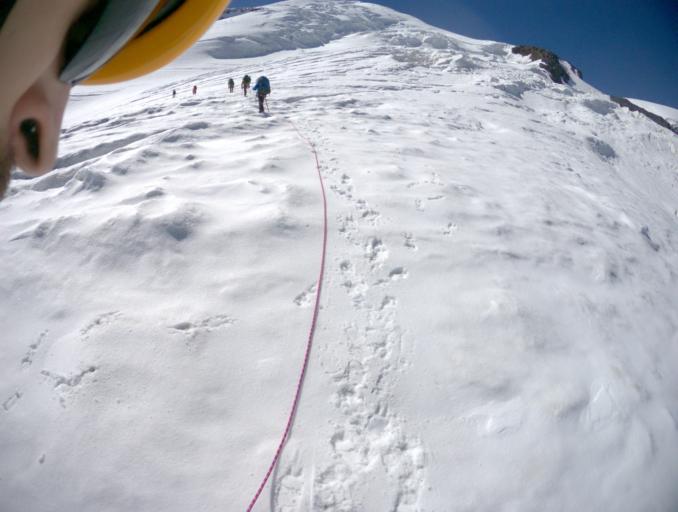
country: RU
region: Kabardino-Balkariya
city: Terskol
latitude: 43.3825
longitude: 42.4383
